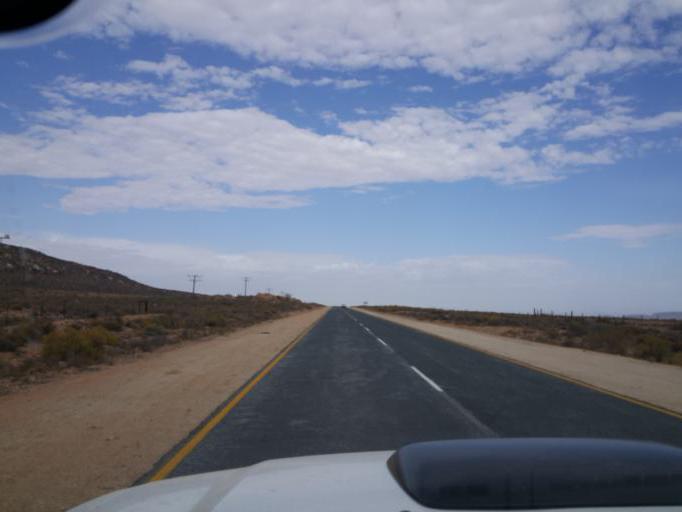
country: ZA
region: Northern Cape
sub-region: Namakwa District Municipality
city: Springbok
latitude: -29.2283
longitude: 17.6791
